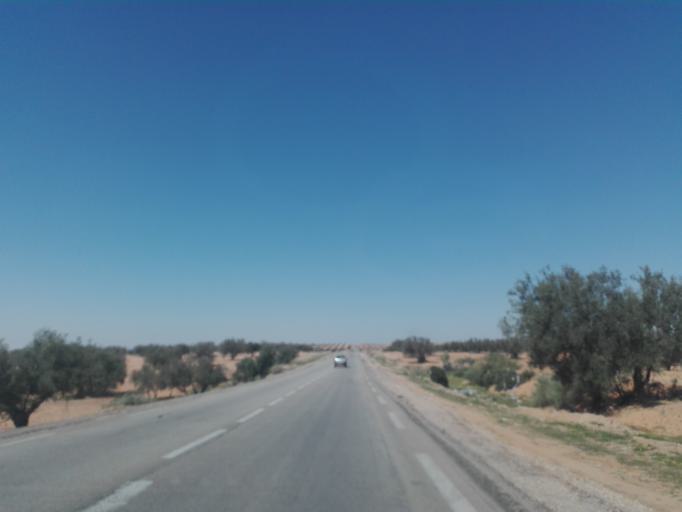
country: TN
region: Safaqis
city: Bi'r `Ali Bin Khalifah
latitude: 34.7587
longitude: 10.2986
